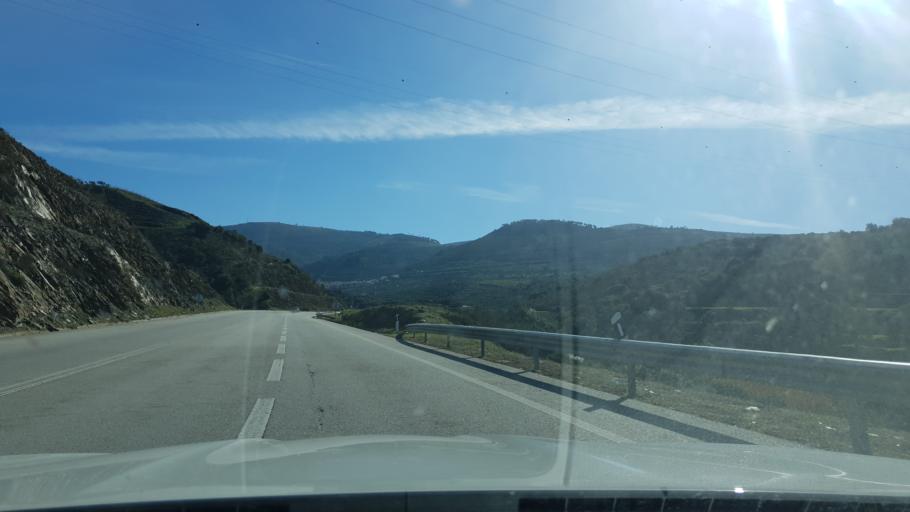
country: PT
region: Braganca
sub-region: Torre de Moncorvo
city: Torre de Moncorvo
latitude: 41.1801
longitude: -7.0770
